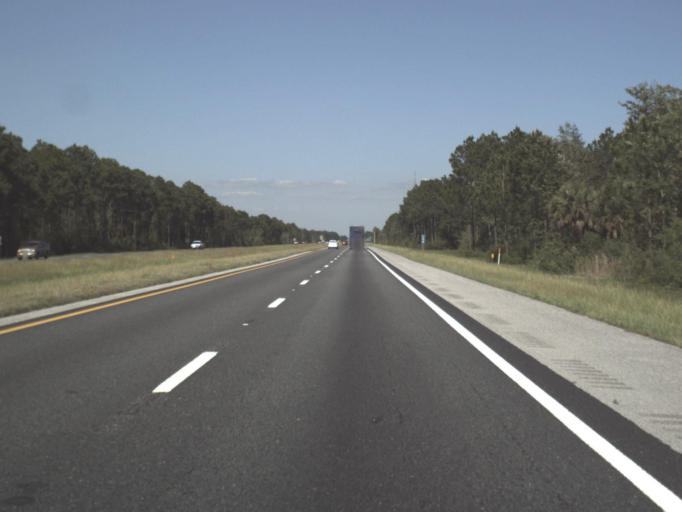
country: US
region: Florida
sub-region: Santa Rosa County
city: Bagdad
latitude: 30.5507
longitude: -87.0561
